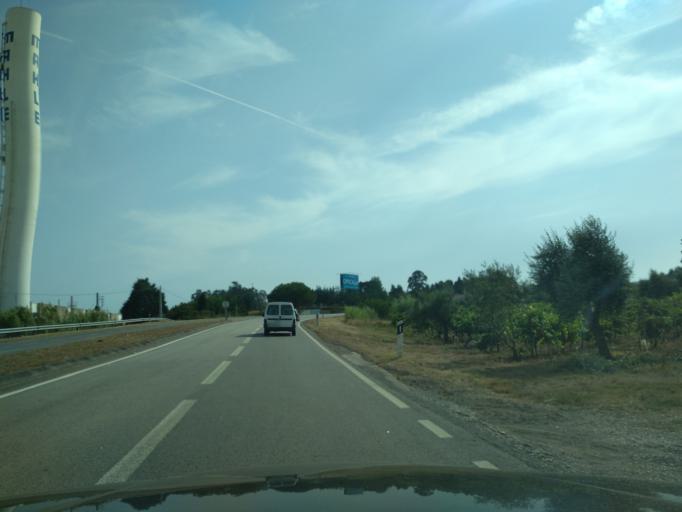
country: PT
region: Aveiro
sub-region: Mealhada
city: Mealhada
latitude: 40.3669
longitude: -8.4908
